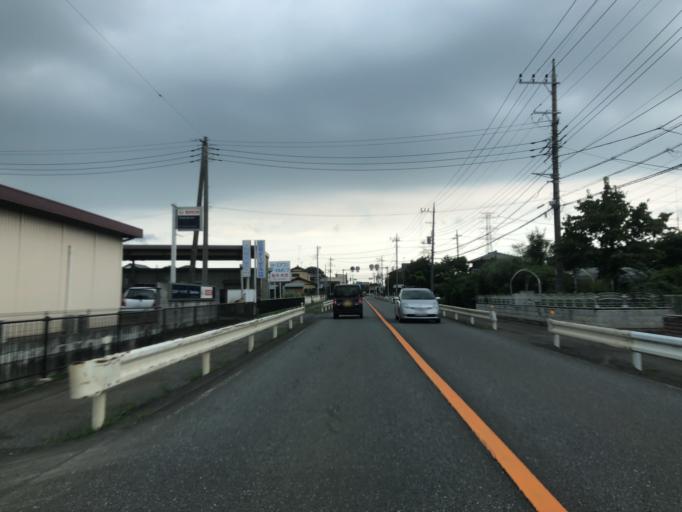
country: JP
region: Saitama
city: Sakado
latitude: 36.0245
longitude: 139.3933
